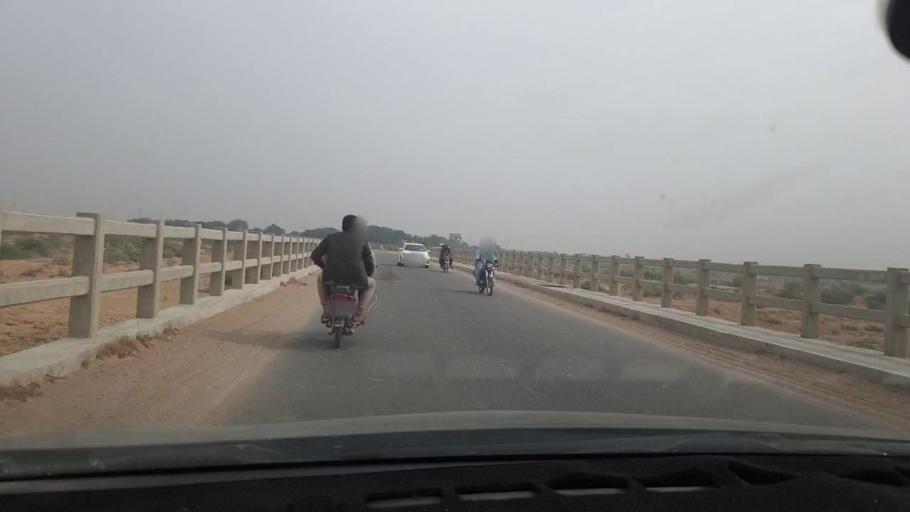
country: PK
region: Sindh
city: Malir Cantonment
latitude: 24.9144
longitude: 67.2665
